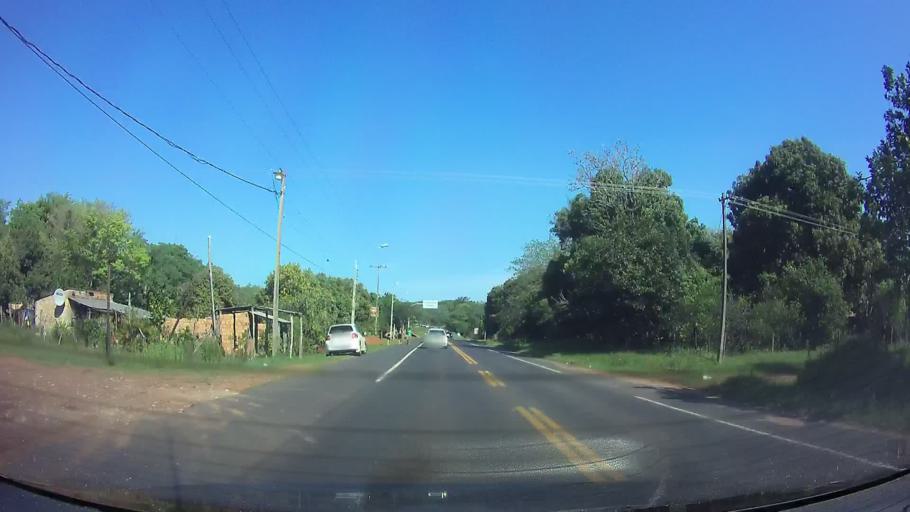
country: PY
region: Central
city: Itaugua
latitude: -25.3522
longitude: -57.3356
